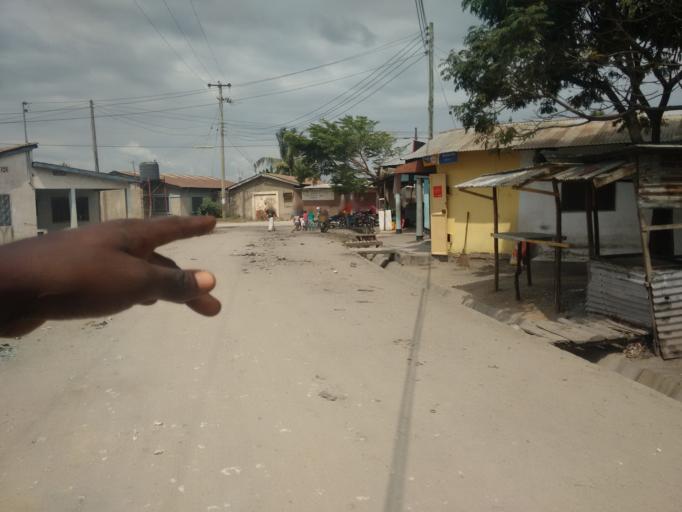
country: TZ
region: Dar es Salaam
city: Dar es Salaam
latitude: -6.8557
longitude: 39.2514
